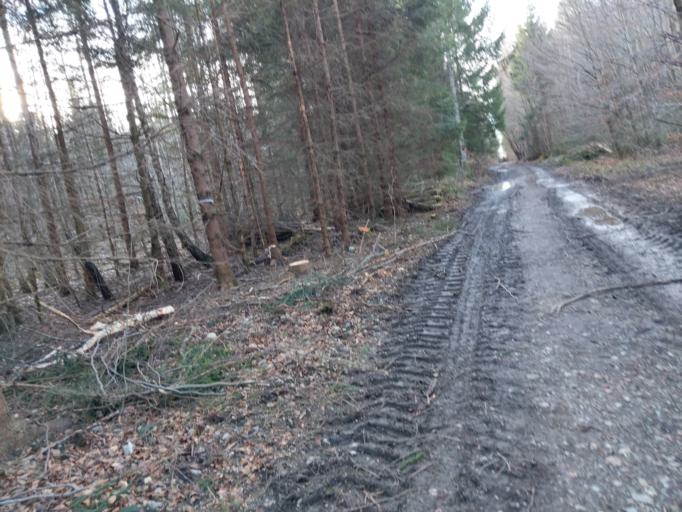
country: DE
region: Bavaria
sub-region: Upper Bavaria
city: Zorneding
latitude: 48.0972
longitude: 11.8466
